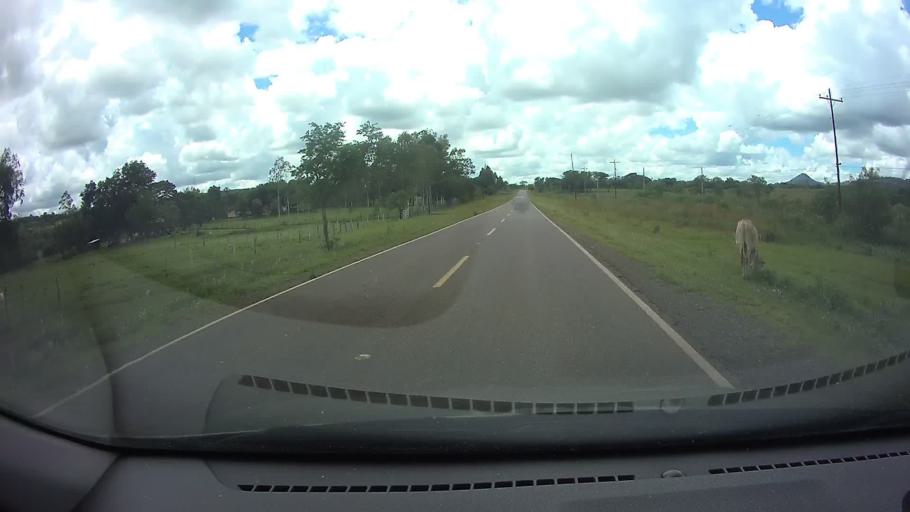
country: PY
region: Paraguari
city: La Colmena
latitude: -25.8967
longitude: -56.9575
